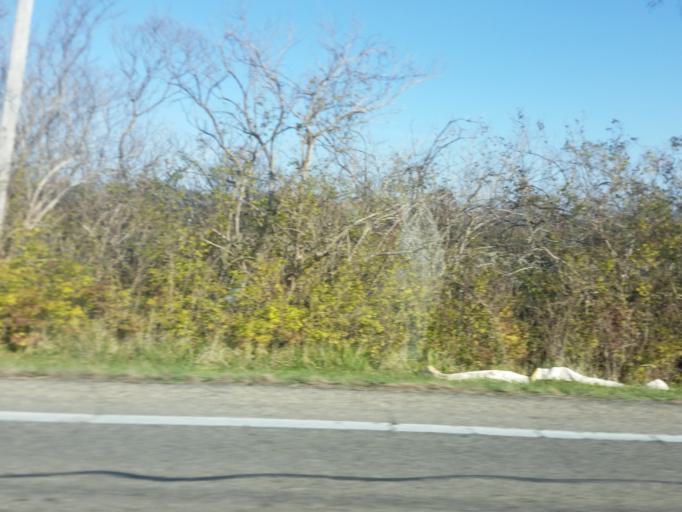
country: US
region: Ohio
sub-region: Butler County
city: Oxford
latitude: 39.4754
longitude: -84.7086
